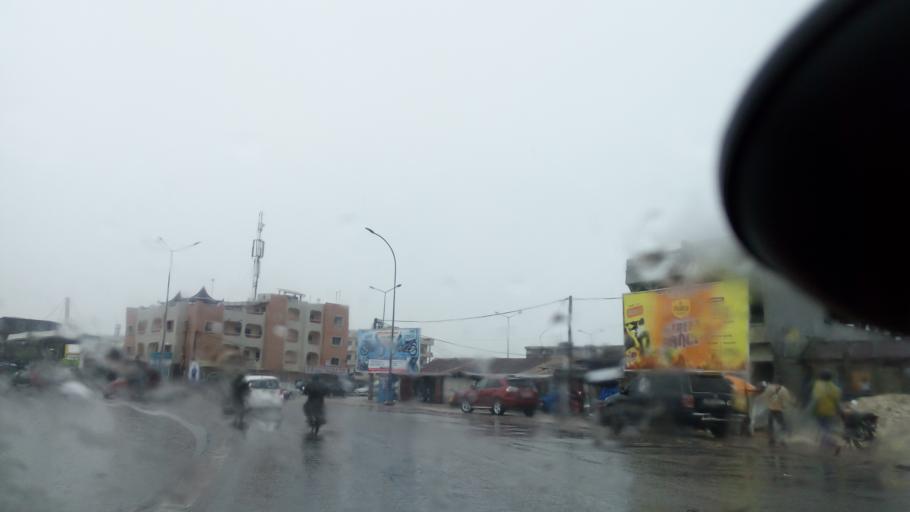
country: BJ
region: Littoral
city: Cotonou
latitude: 6.3708
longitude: 2.4097
